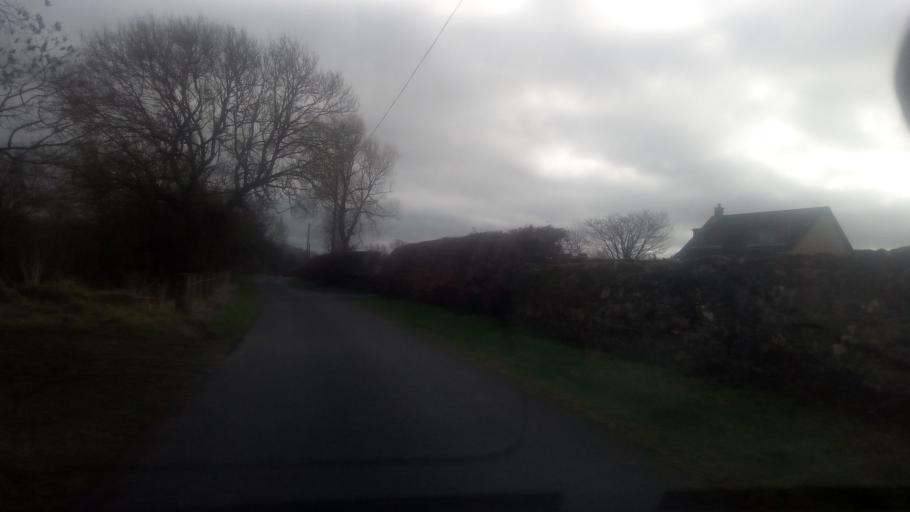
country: GB
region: Scotland
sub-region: The Scottish Borders
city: Kelso
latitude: 55.5427
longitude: -2.4682
